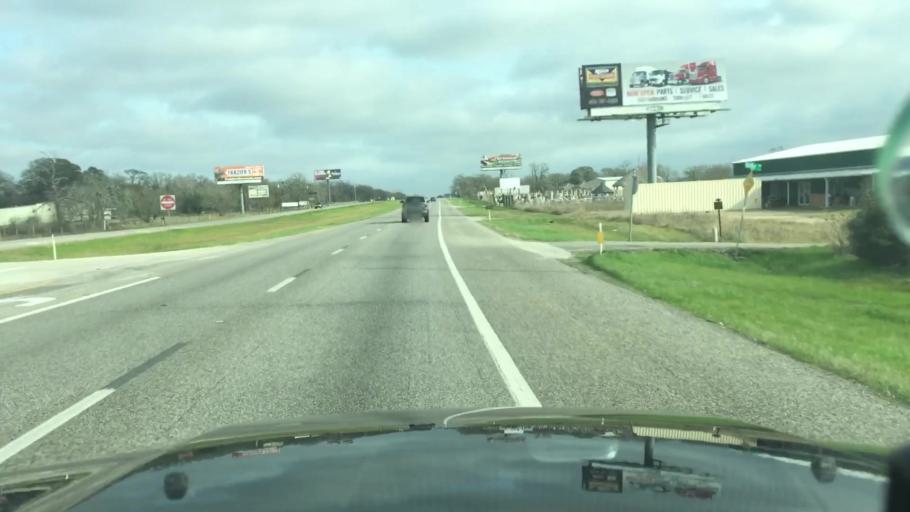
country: US
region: Texas
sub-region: Waller County
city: Hempstead
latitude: 30.1302
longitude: -96.1378
